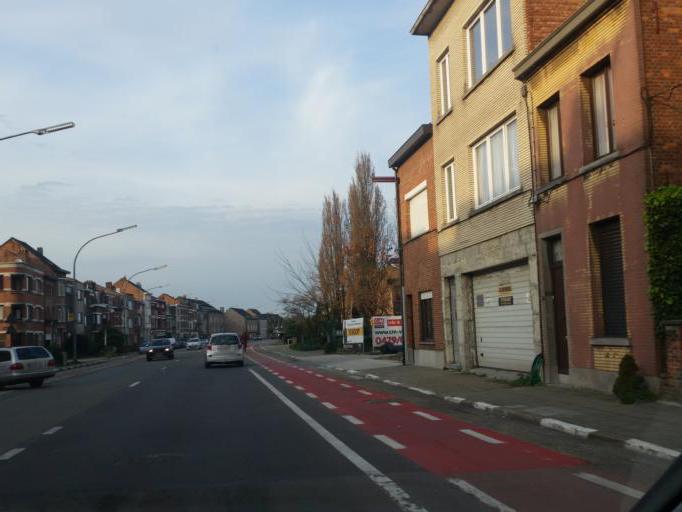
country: BE
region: Flanders
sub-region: Provincie Antwerpen
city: Mechelen
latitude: 51.0390
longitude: 4.4800
